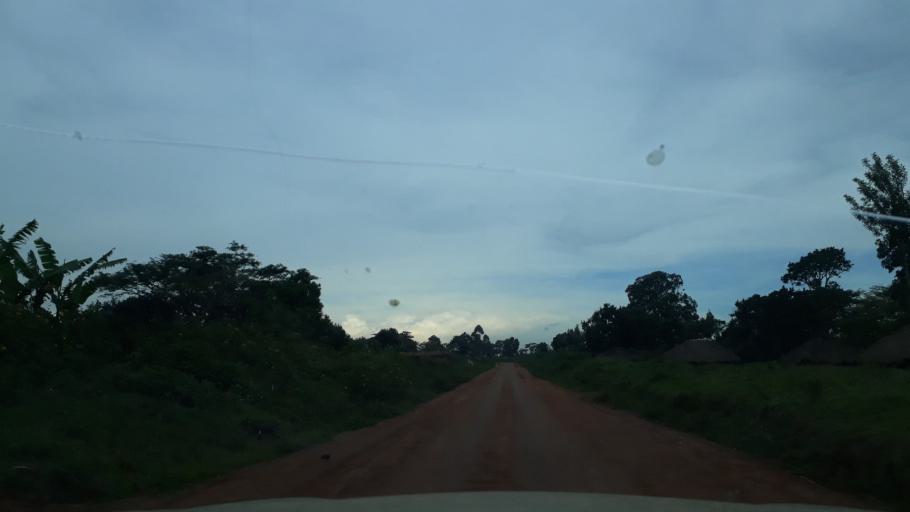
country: UG
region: Northern Region
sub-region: Zombo District
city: Paidha
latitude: 2.1765
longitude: 30.7128
